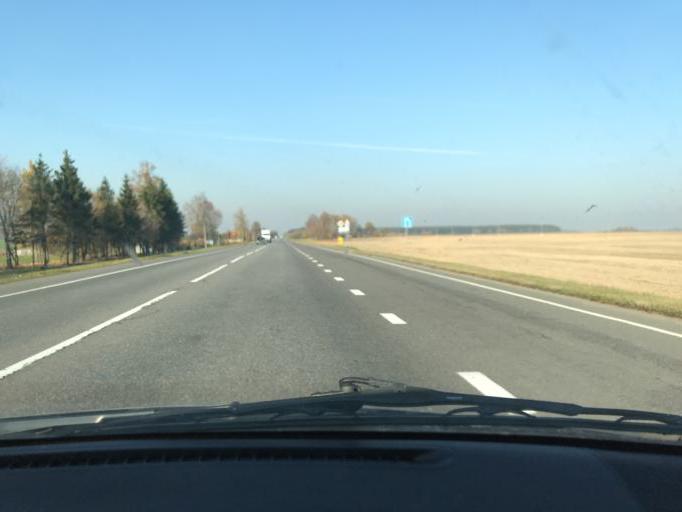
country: BY
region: Mogilev
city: Shklow
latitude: 54.2719
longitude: 30.4497
